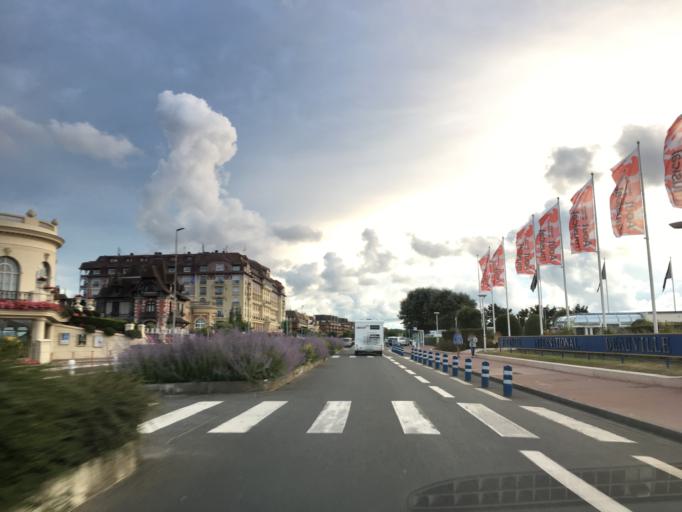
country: FR
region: Lower Normandy
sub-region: Departement du Calvados
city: Deauville
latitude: 49.3599
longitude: 0.0696
